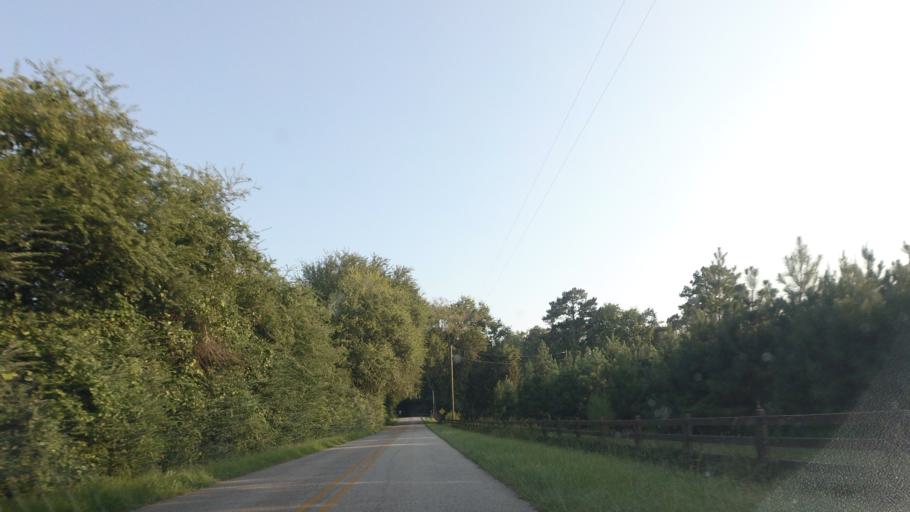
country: US
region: Georgia
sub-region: Bibb County
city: West Point
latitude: 32.9305
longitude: -83.8073
